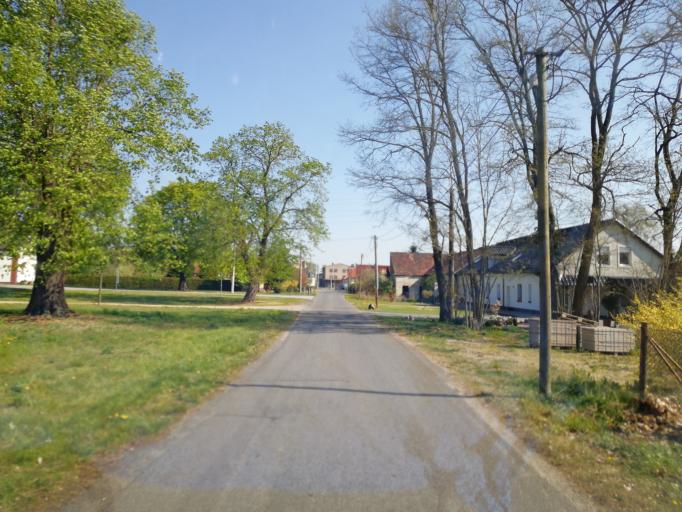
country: DE
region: Brandenburg
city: Calau
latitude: 51.7860
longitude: 13.8794
